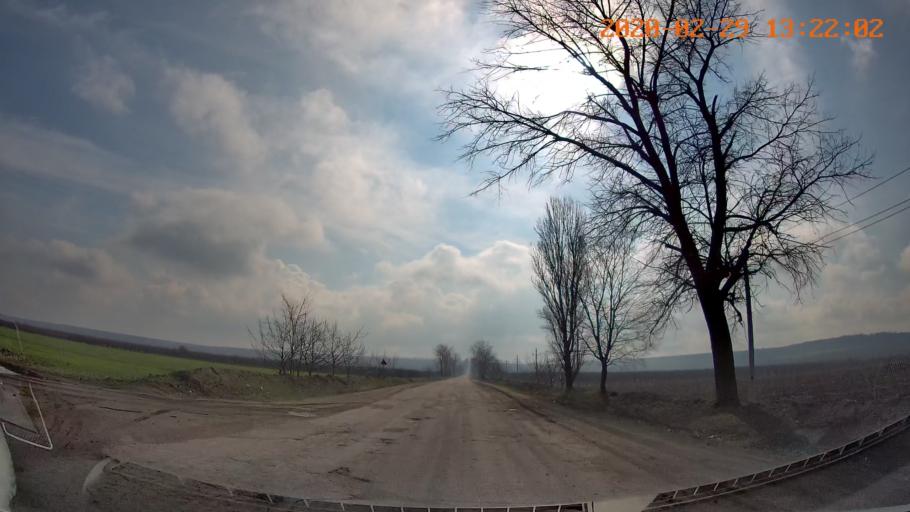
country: MD
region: Telenesti
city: Camenca
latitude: 47.9648
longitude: 28.6287
